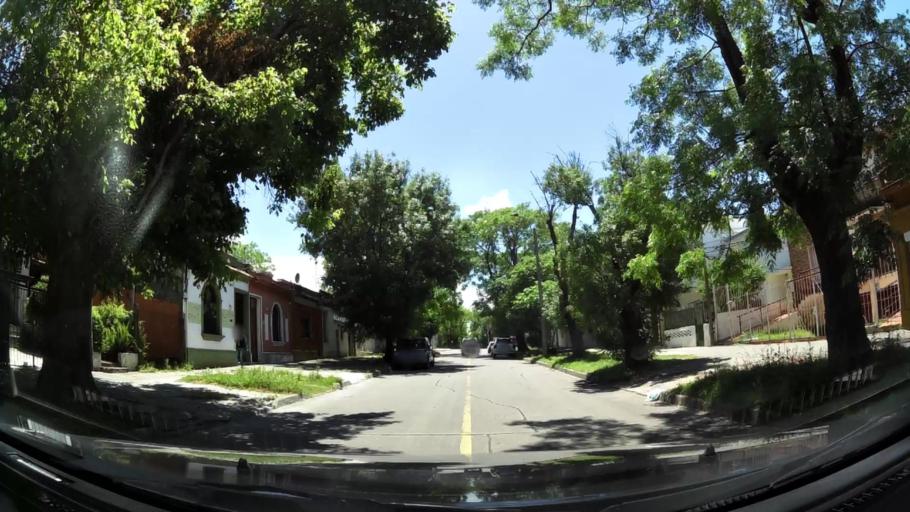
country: UY
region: Montevideo
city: Montevideo
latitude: -34.8976
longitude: -56.1360
